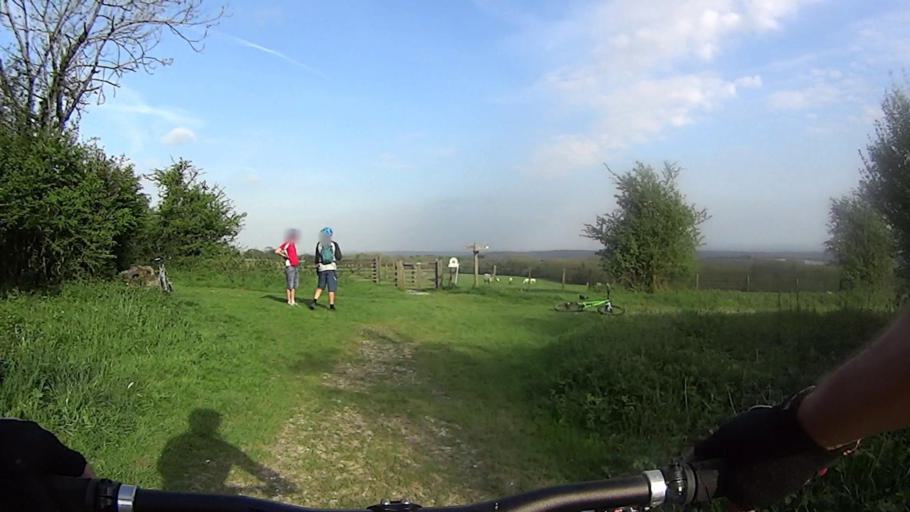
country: GB
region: England
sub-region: West Sussex
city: Fontwell
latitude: 50.9074
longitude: -0.6324
